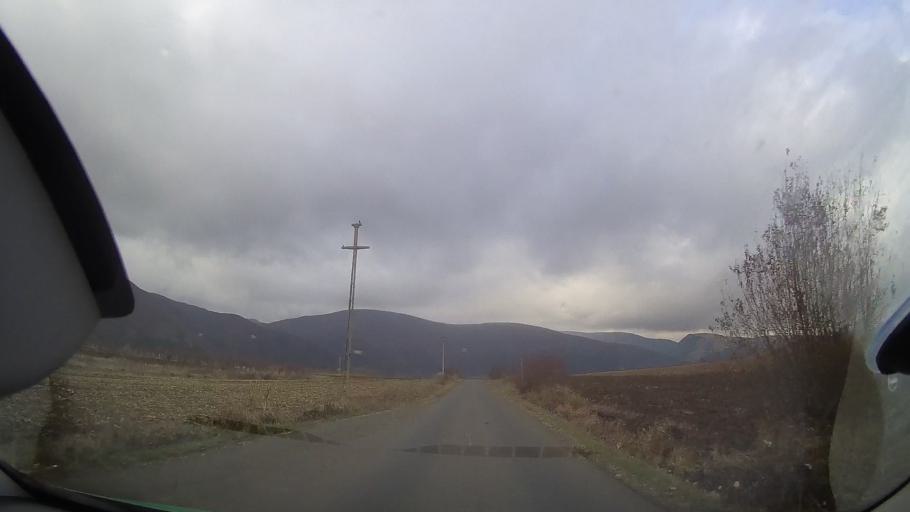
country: RO
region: Cluj
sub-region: Comuna Moldovenesti
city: Moldovenesti
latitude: 46.5059
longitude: 23.6744
